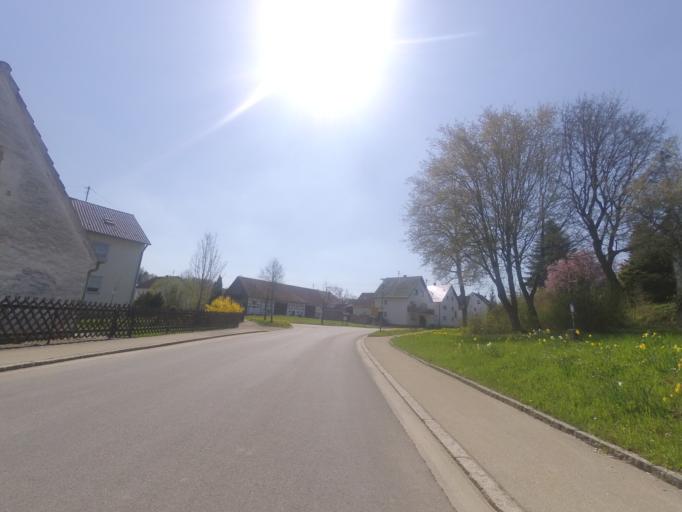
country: DE
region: Bavaria
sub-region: Swabia
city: Roggenburg
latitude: 48.3137
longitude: 10.2113
